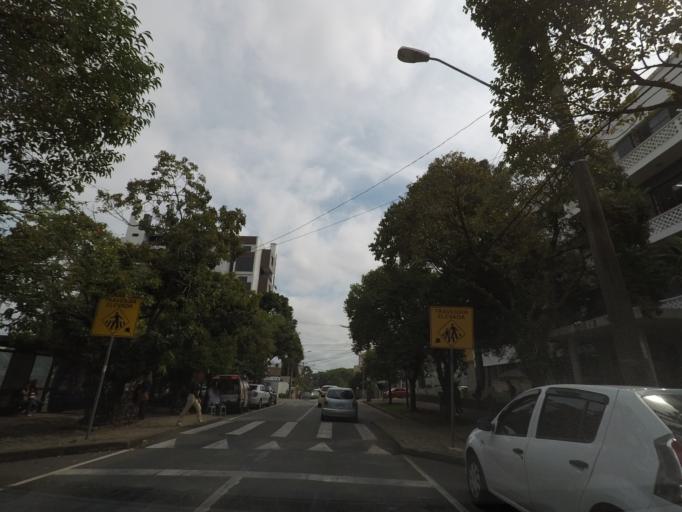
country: BR
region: Parana
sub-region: Curitiba
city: Curitiba
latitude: -25.4540
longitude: -49.2923
